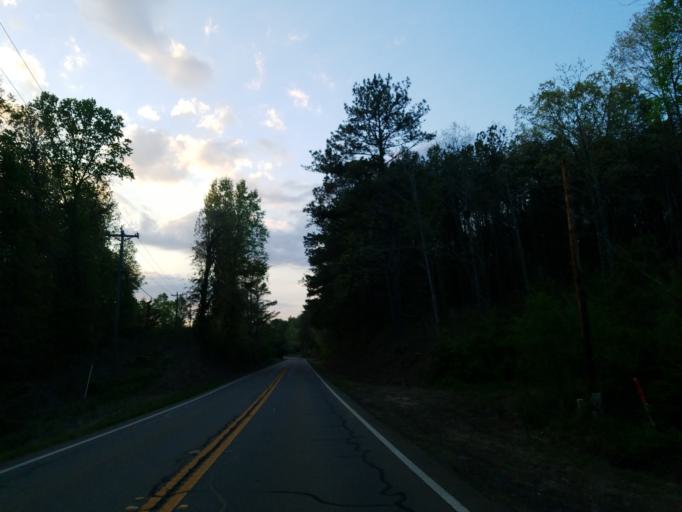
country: US
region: Georgia
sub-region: Pickens County
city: Jasper
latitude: 34.5201
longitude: -84.4679
